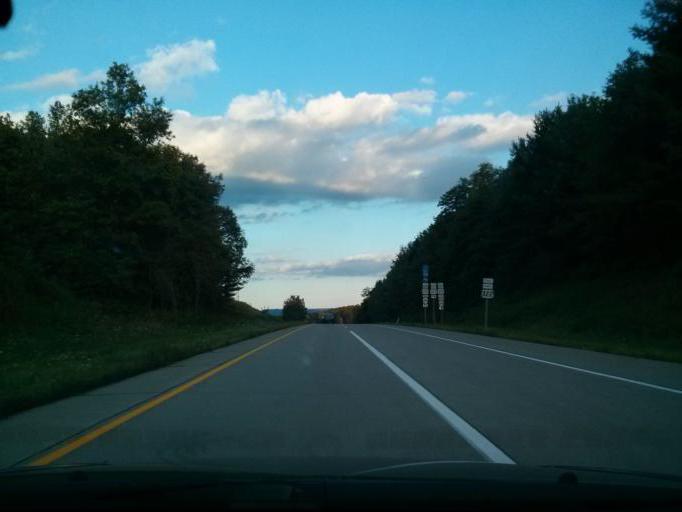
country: US
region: Pennsylvania
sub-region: Centre County
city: Park Forest Village
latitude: 40.8147
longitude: -77.9286
